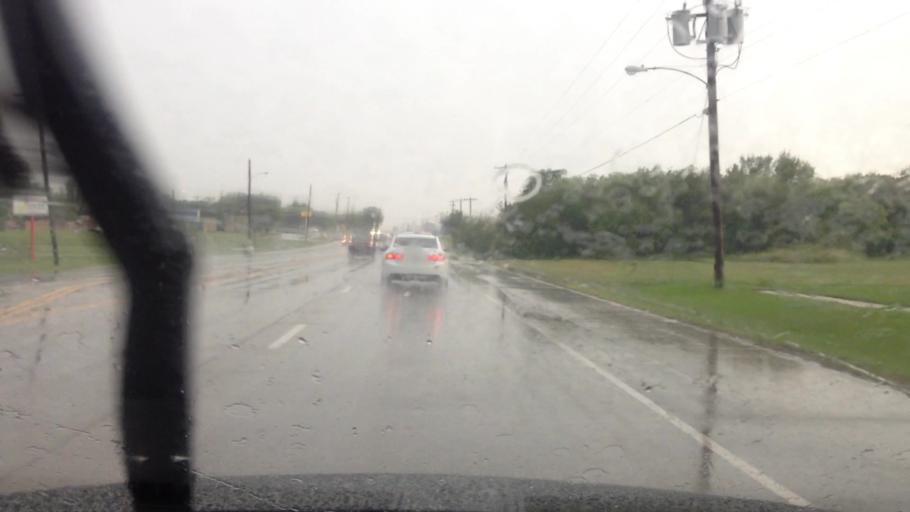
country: US
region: Texas
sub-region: Tarrant County
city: North Richland Hills
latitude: 32.8410
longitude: -97.2048
